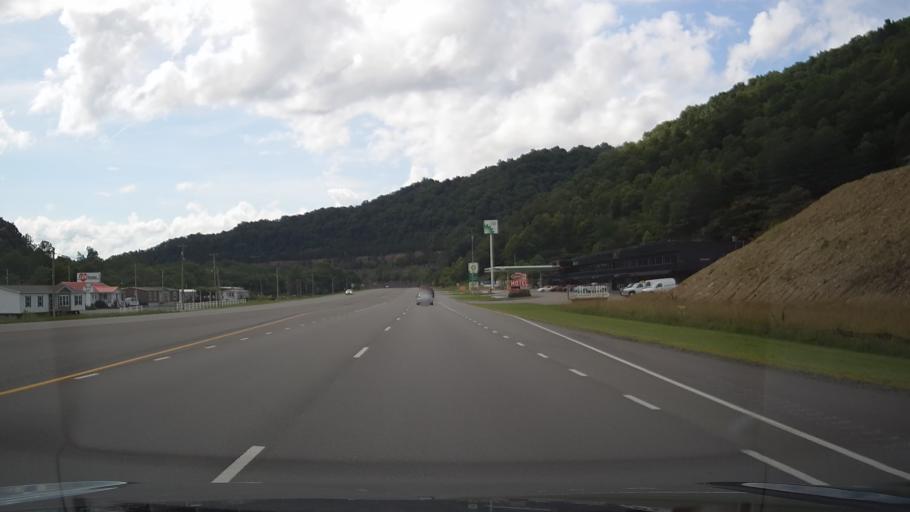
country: US
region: Kentucky
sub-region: Floyd County
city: Prestonsburg
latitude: 37.5979
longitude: -82.6820
